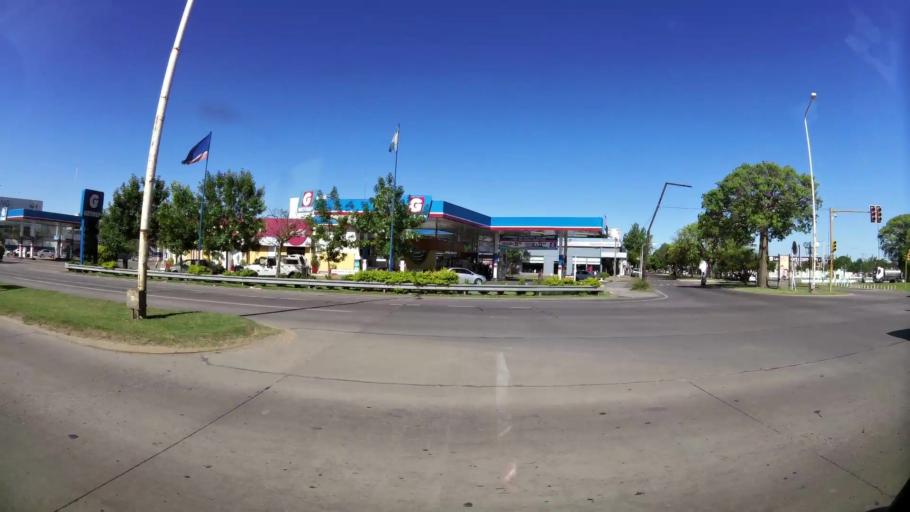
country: AR
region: Santa Fe
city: Rafaela
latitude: -31.2505
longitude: -61.5059
